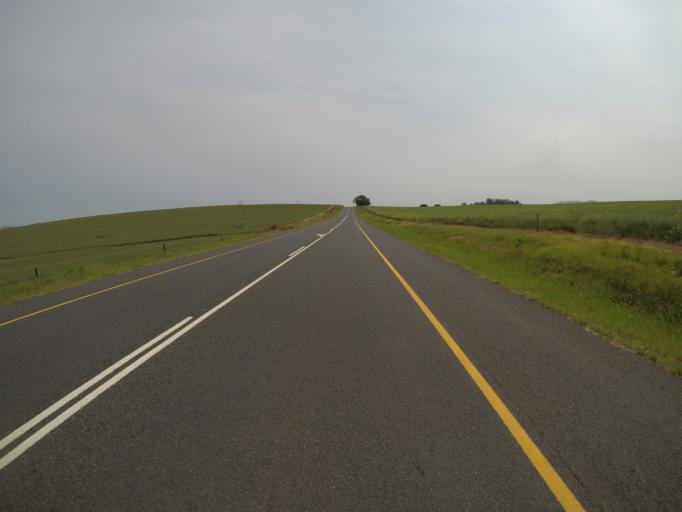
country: ZA
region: Western Cape
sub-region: West Coast District Municipality
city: Malmesbury
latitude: -33.5074
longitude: 18.8413
